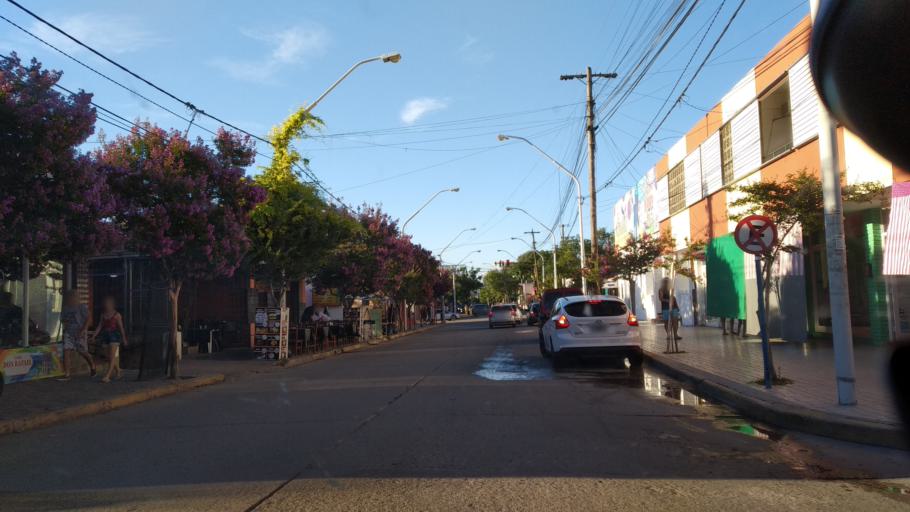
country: AR
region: Cordoba
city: Mina Clavero
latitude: -31.7200
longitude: -65.0048
